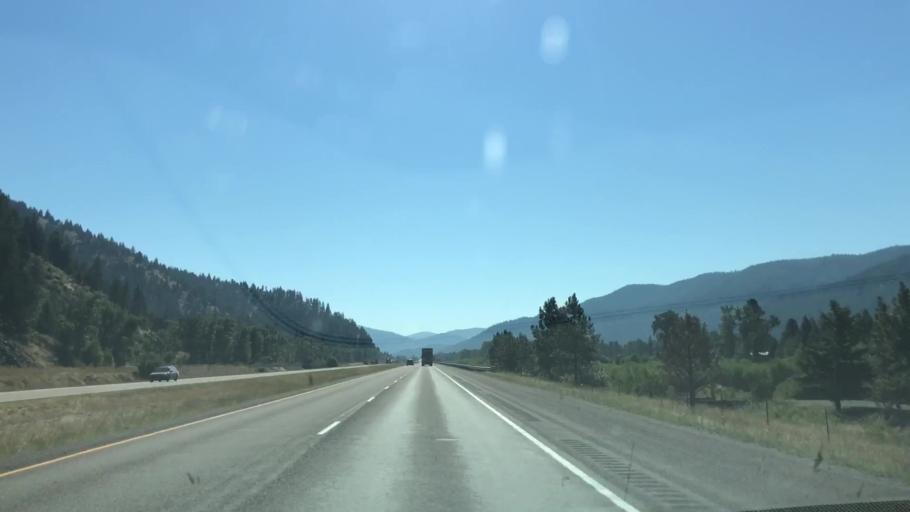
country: US
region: Montana
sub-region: Missoula County
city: Bonner-West Riverside
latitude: 46.8234
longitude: -113.8076
